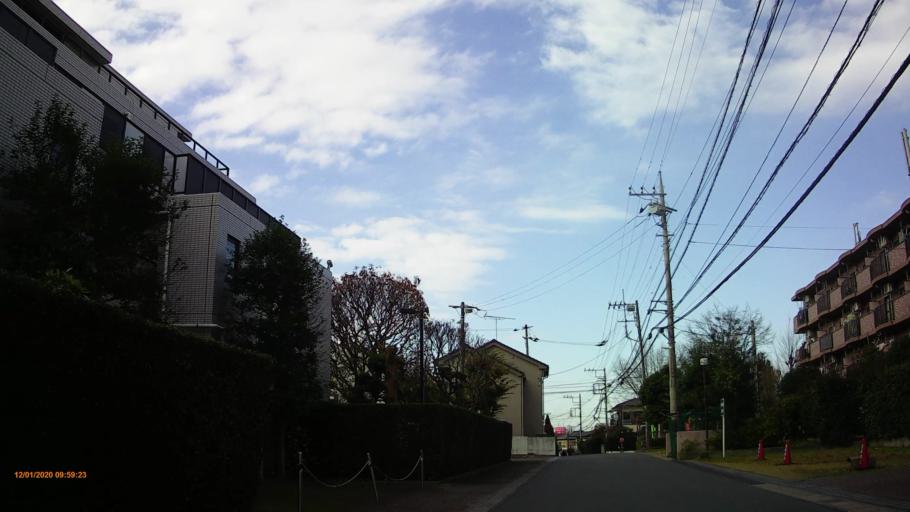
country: JP
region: Chiba
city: Yotsukaido
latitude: 35.6331
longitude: 140.1709
